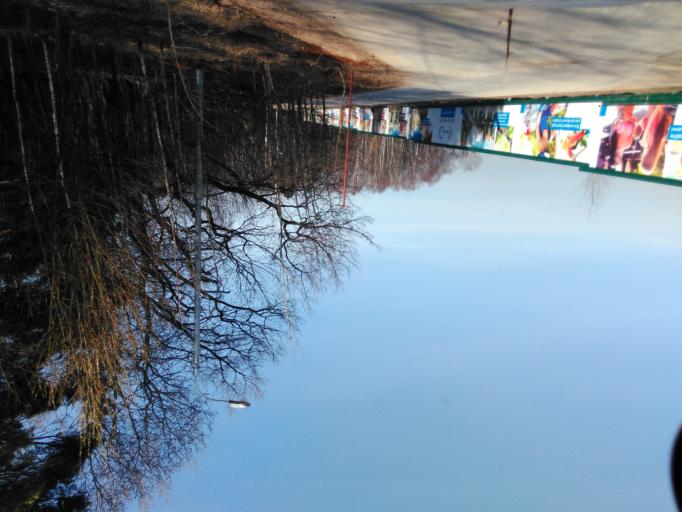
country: RU
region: Moskovskaya
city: Opalikha
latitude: 55.8727
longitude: 37.2614
